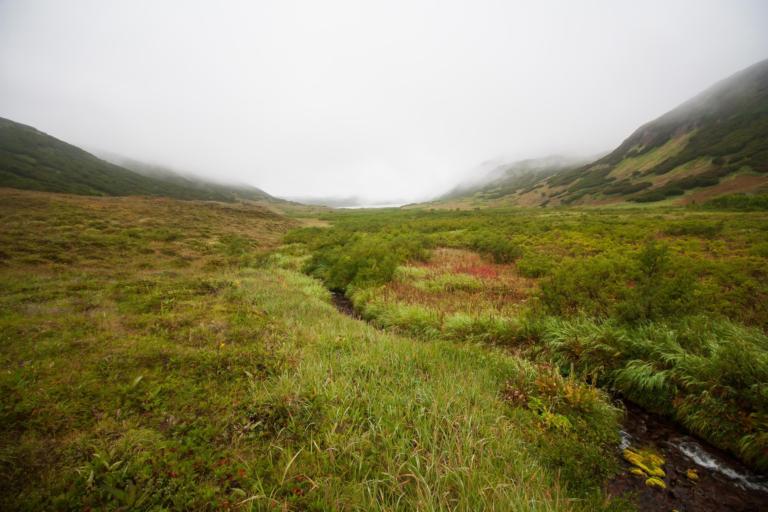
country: RU
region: Kamtsjatka
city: Yelizovo
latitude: 53.9626
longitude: 158.0821
